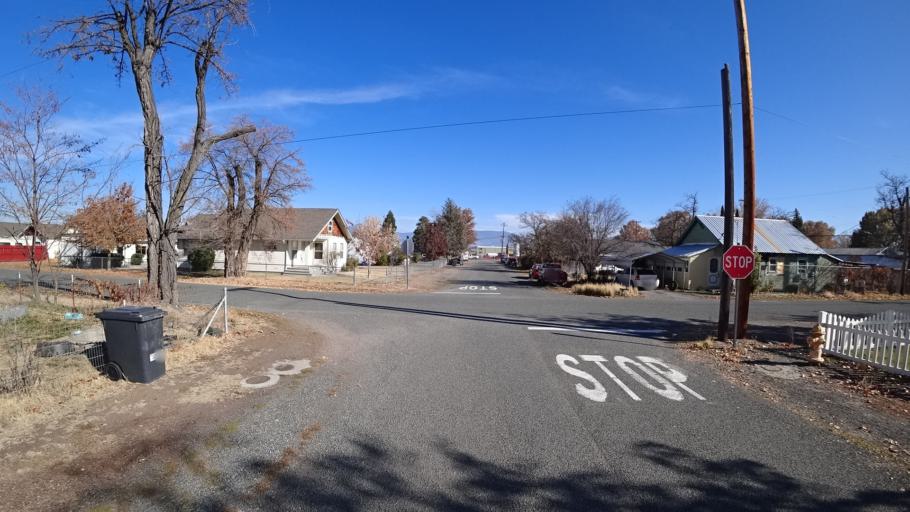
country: US
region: California
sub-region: Siskiyou County
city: Montague
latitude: 41.6464
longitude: -122.5239
